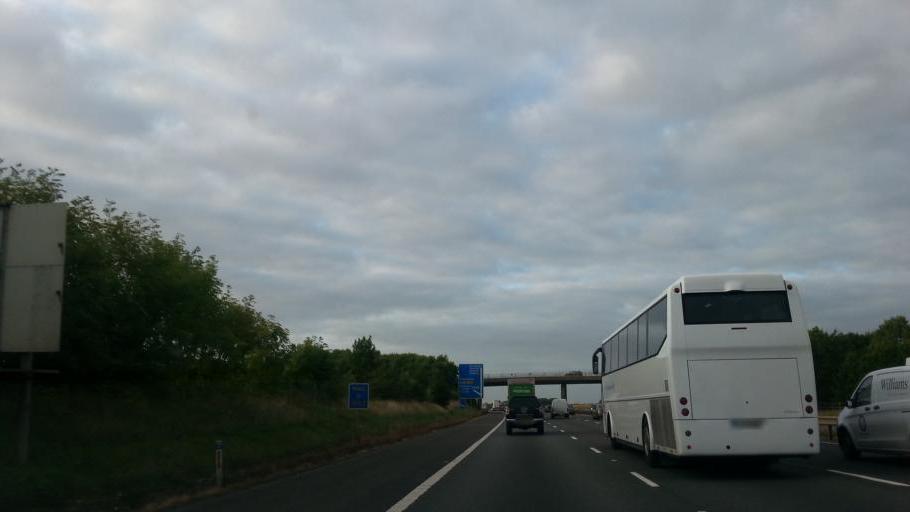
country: GB
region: England
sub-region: Oxfordshire
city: Bicester
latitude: 51.9390
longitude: -1.2022
